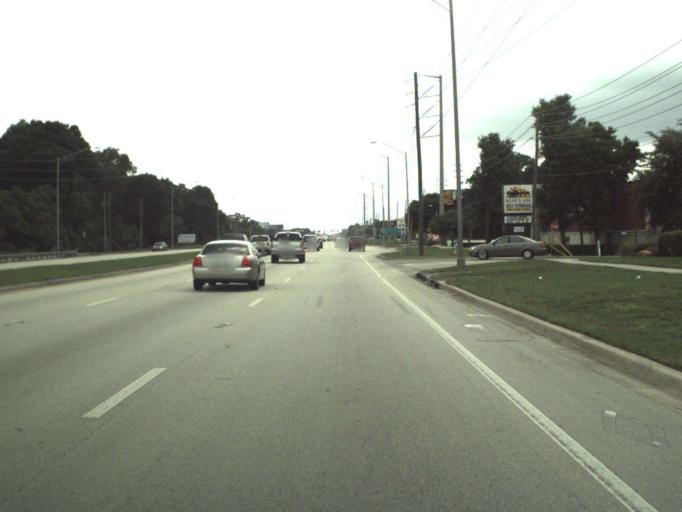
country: US
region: Florida
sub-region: Seminole County
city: Forest City
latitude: 28.6730
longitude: -81.4615
